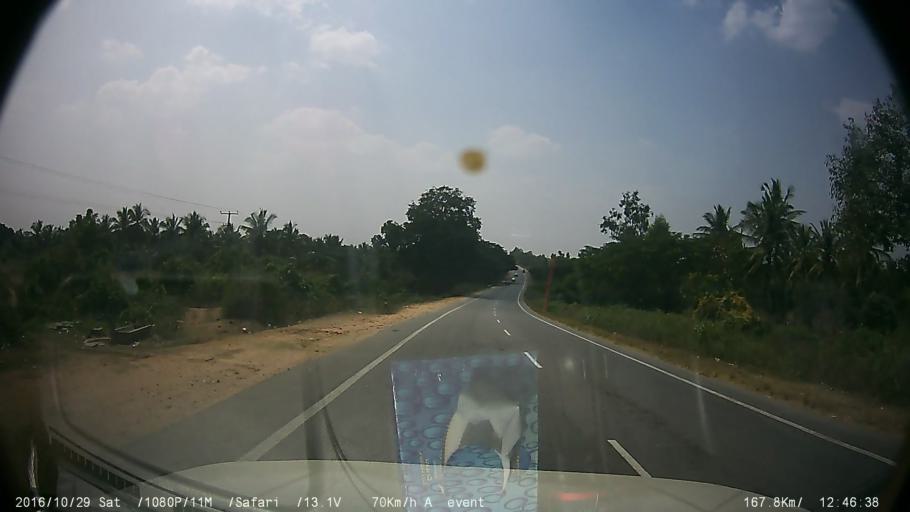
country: IN
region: Karnataka
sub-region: Mysore
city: Hunsur
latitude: 12.3391
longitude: 76.3945
